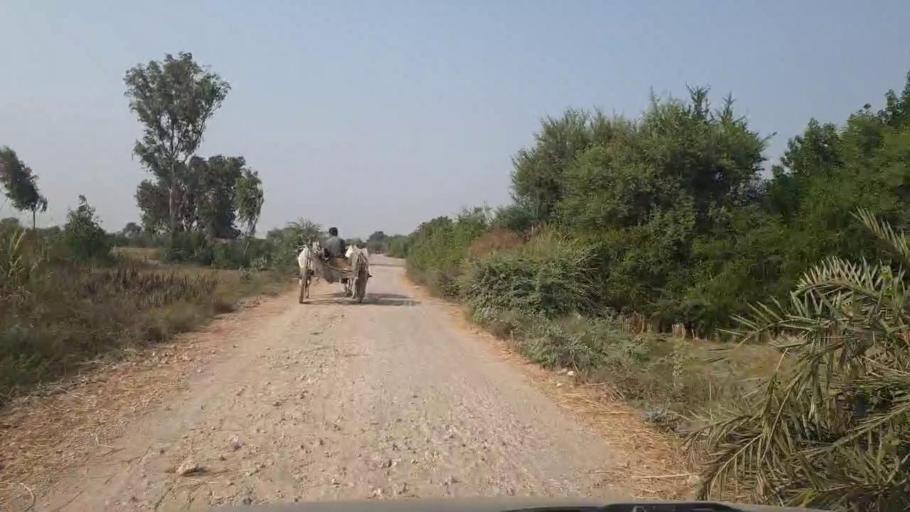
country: PK
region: Sindh
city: Tando Muhammad Khan
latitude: 25.0802
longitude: 68.3438
